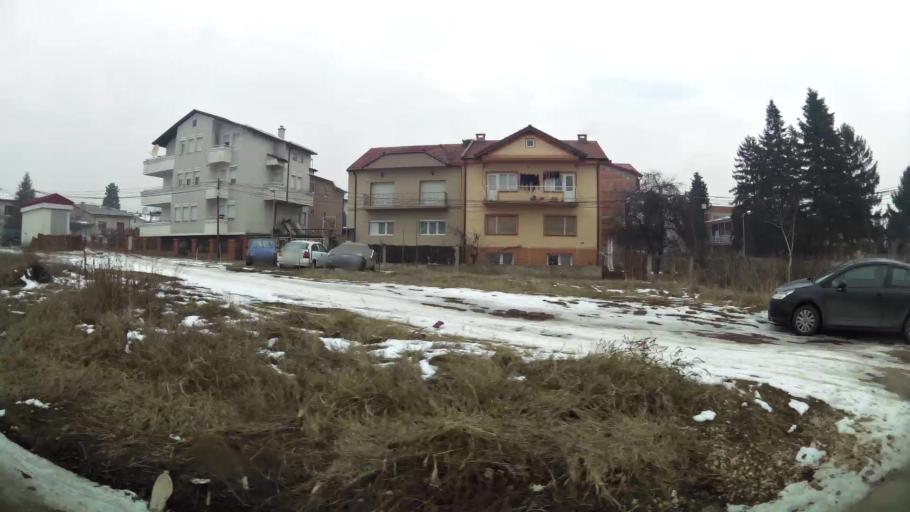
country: MK
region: Cair
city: Cair
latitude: 42.0169
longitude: 21.4504
